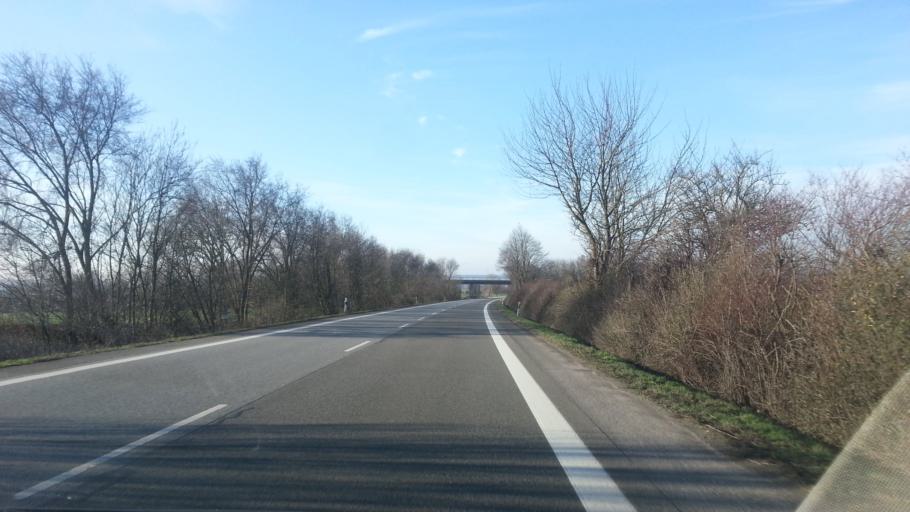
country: DE
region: Rheinland-Pfalz
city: Offstein
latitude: 49.6234
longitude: 8.2677
